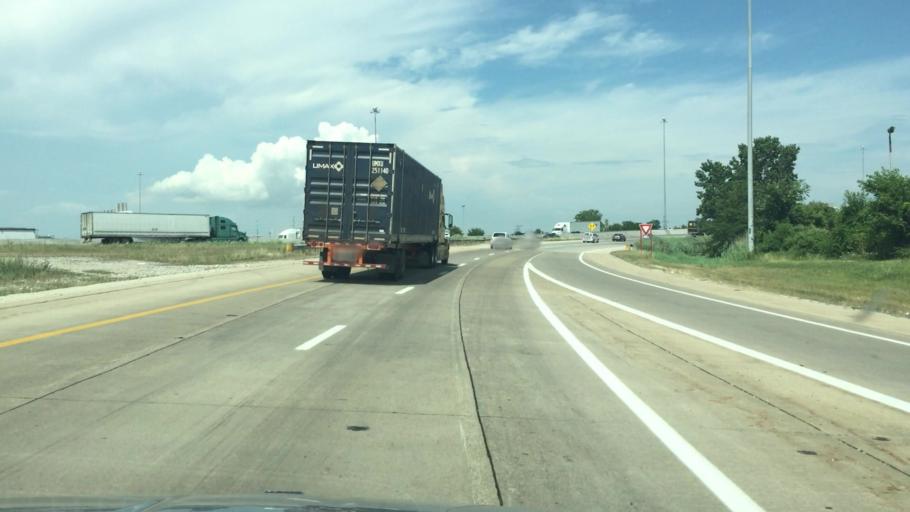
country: US
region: Ohio
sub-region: Lucas County
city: Toledo
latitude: 41.6894
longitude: -83.5146
